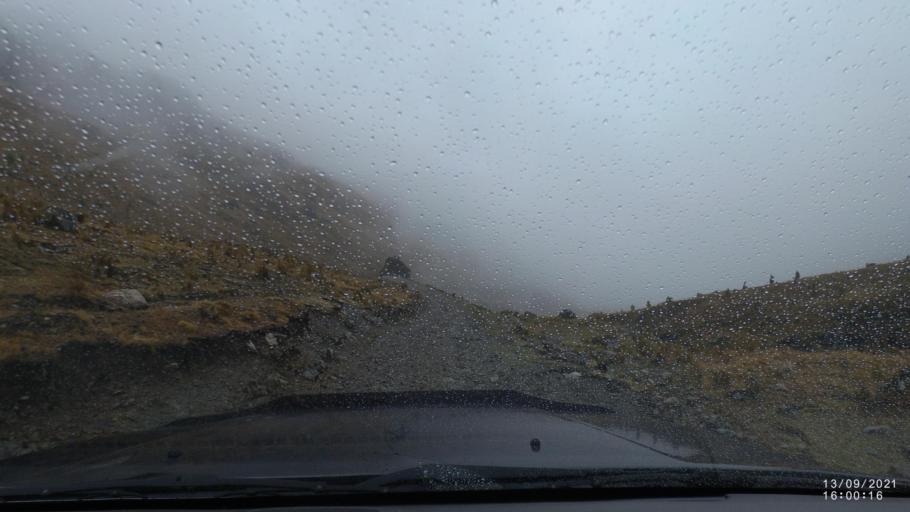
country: BO
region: Cochabamba
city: Colomi
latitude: -17.2960
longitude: -65.7081
